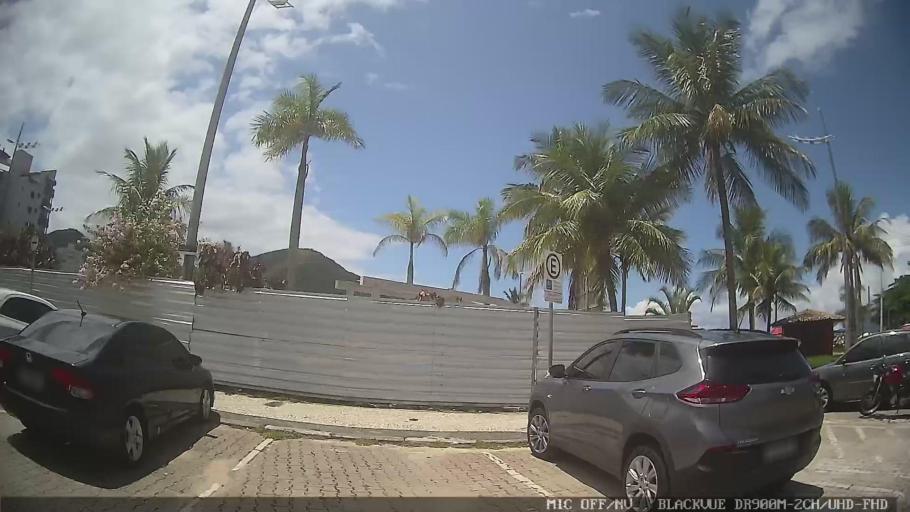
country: BR
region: Sao Paulo
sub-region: Caraguatatuba
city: Caraguatatuba
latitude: -23.6270
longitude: -45.3832
